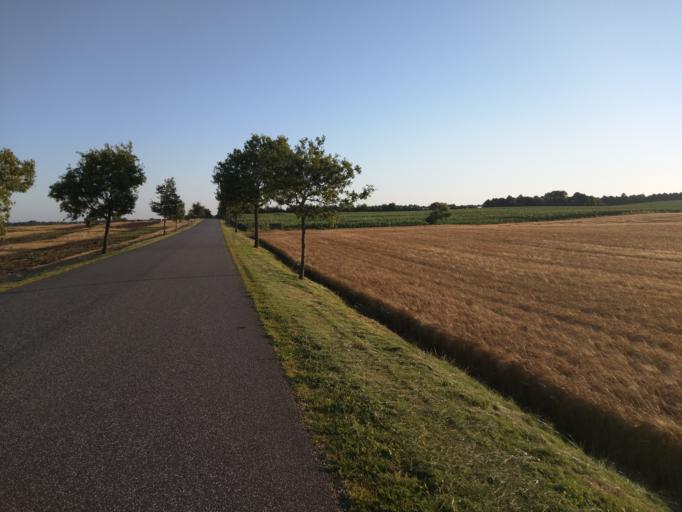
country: DK
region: Central Jutland
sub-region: Viborg Kommune
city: Bjerringbro
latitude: 56.4790
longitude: 9.5763
